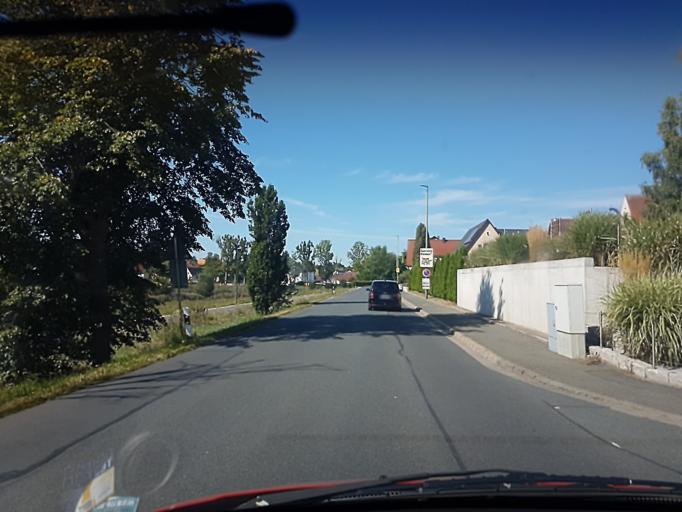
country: DE
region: Bavaria
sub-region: Upper Franconia
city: Heroldsbach
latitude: 49.6918
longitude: 11.0091
